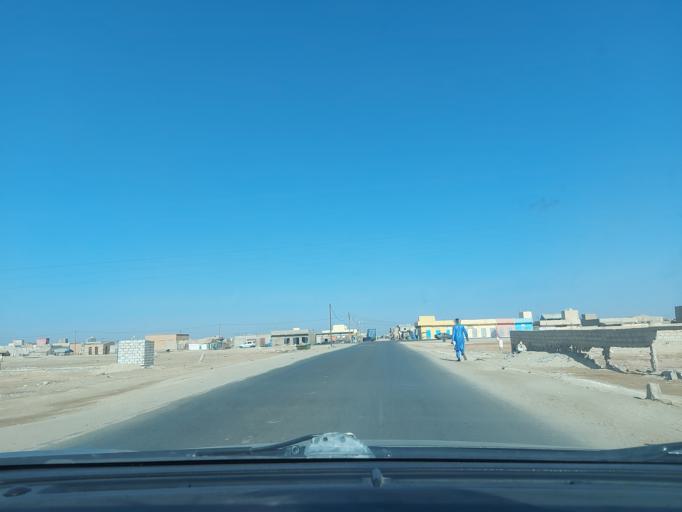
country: MR
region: Nouakchott
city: Nouakchott
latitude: 18.0116
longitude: -15.9862
